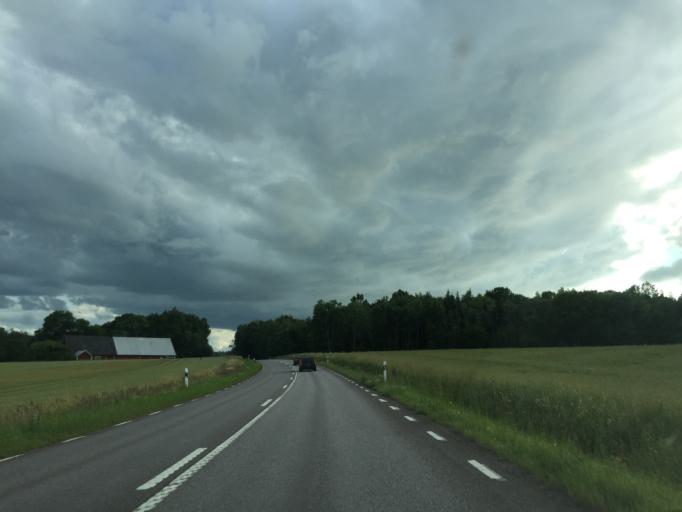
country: SE
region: OEstergoetland
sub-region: Motala Kommun
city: Motala
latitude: 58.4897
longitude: 14.9956
